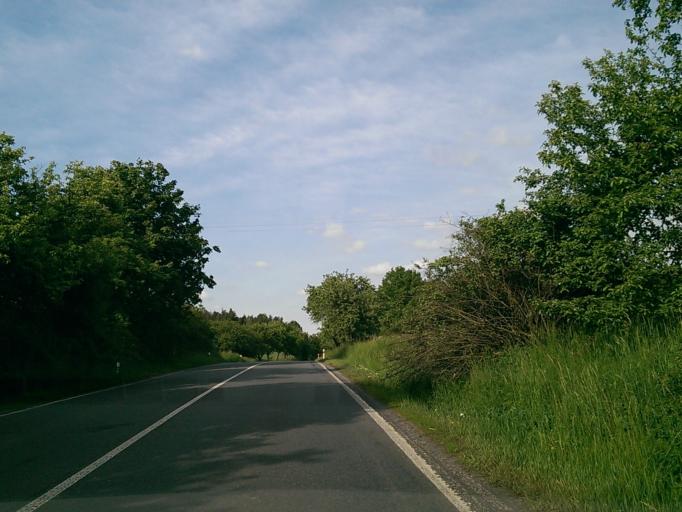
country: CZ
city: Duba
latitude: 50.5318
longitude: 14.5210
